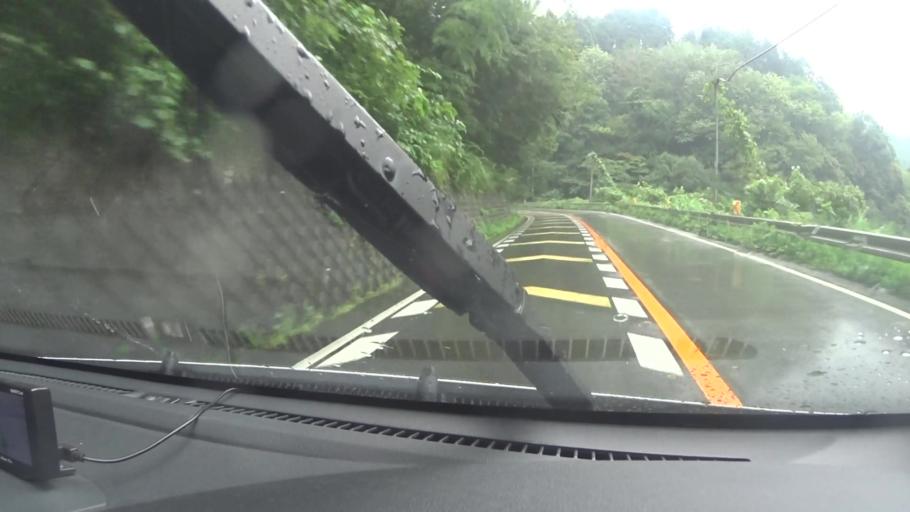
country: JP
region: Kyoto
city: Ayabe
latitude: 35.2229
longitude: 135.3375
